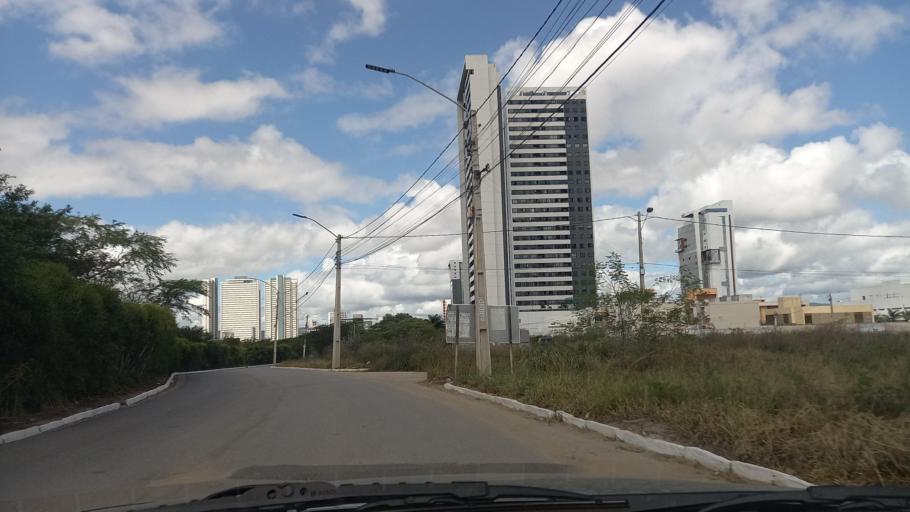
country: BR
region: Pernambuco
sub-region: Caruaru
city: Caruaru
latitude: -8.2558
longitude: -35.9657
